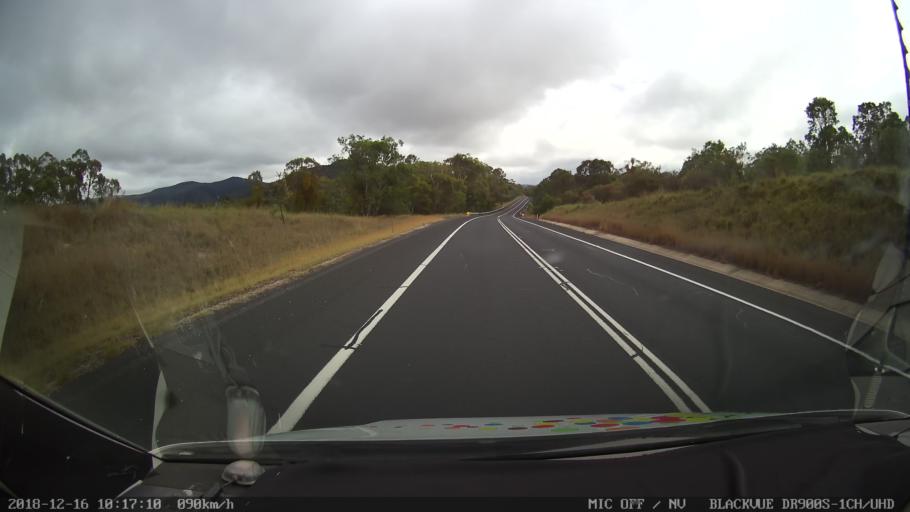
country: AU
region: New South Wales
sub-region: Tenterfield Municipality
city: Carrolls Creek
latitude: -29.2589
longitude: 151.9893
